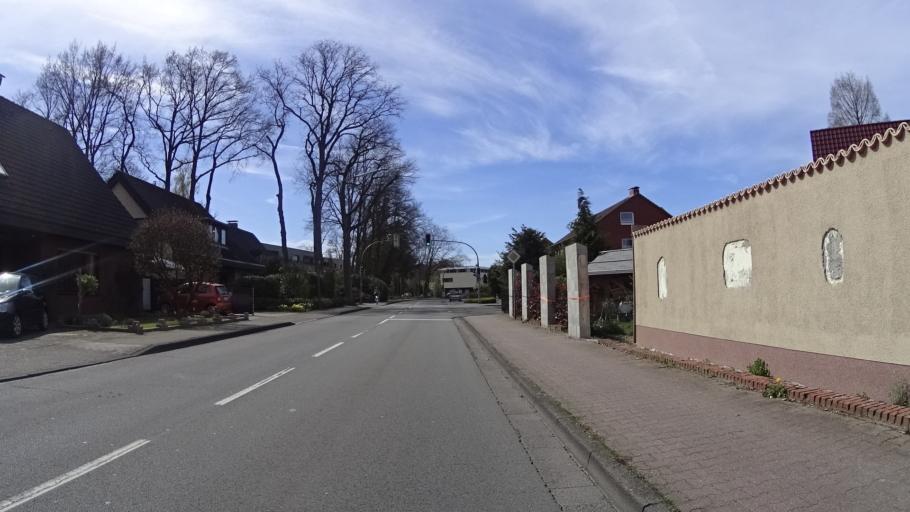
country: DE
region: Lower Saxony
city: Lingen
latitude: 52.5036
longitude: 7.3162
